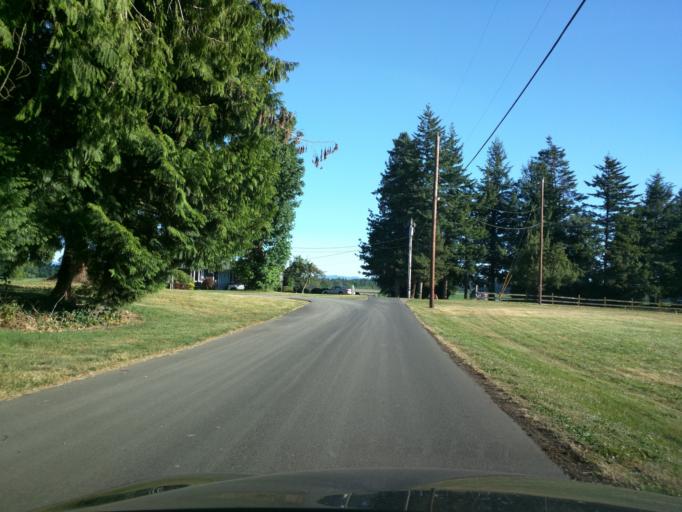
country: US
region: Washington
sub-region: Whatcom County
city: Lynden
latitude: 48.9341
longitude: -122.4775
